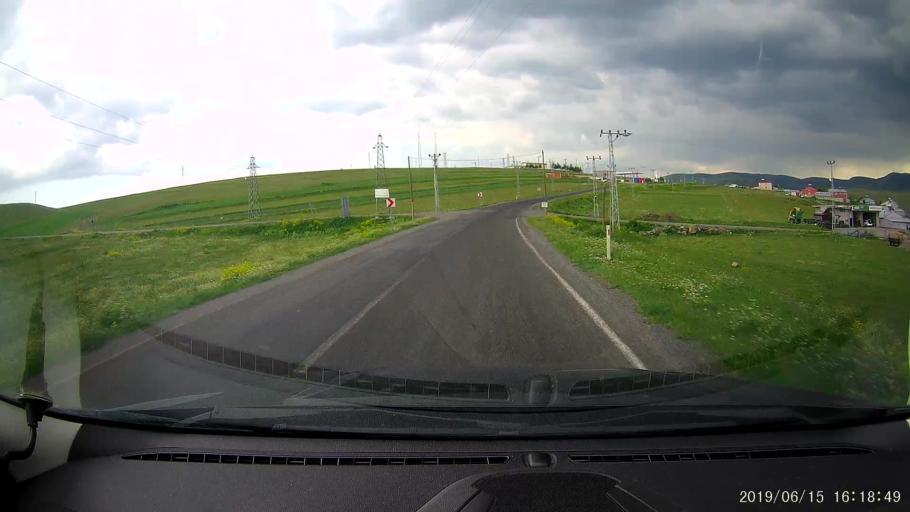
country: TR
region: Ardahan
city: Hanak
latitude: 41.2352
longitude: 42.8529
